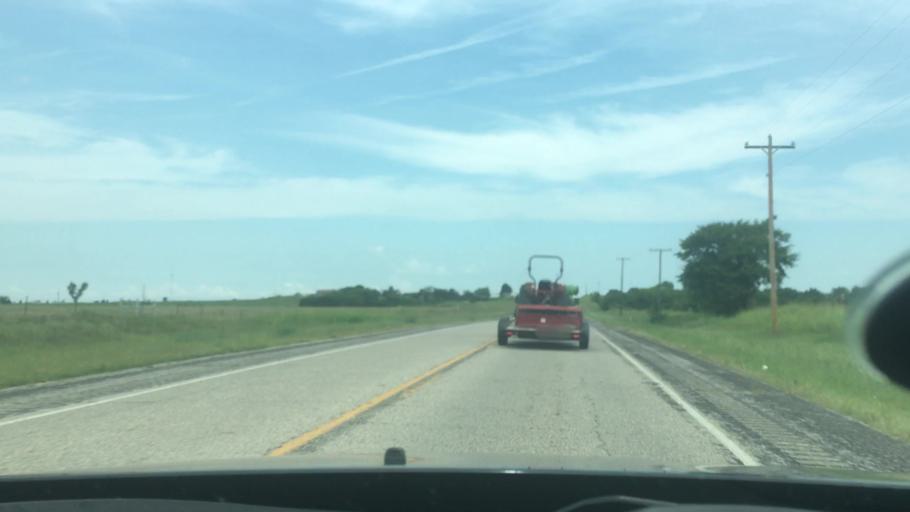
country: US
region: Oklahoma
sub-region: Seminole County
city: Seminole
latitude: 35.2710
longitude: -96.7201
